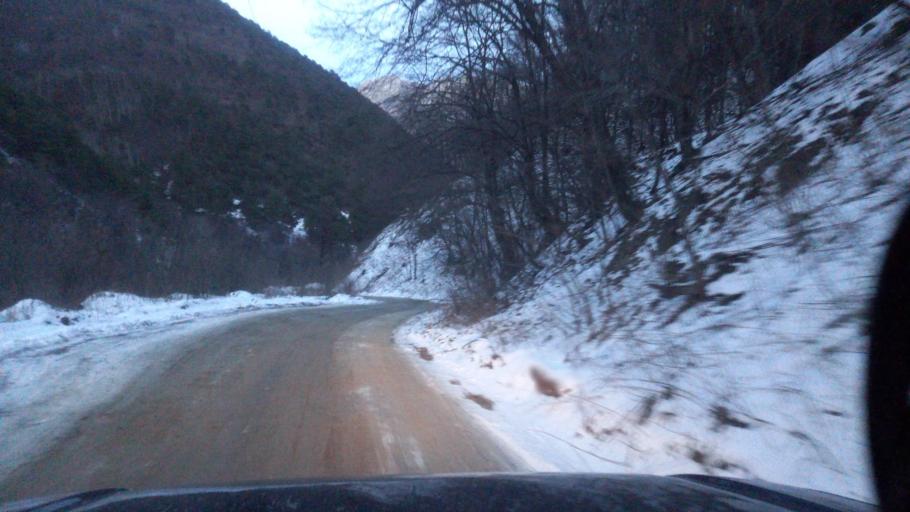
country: RU
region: Ingushetiya
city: Dzhayrakh
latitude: 42.8258
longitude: 44.6015
